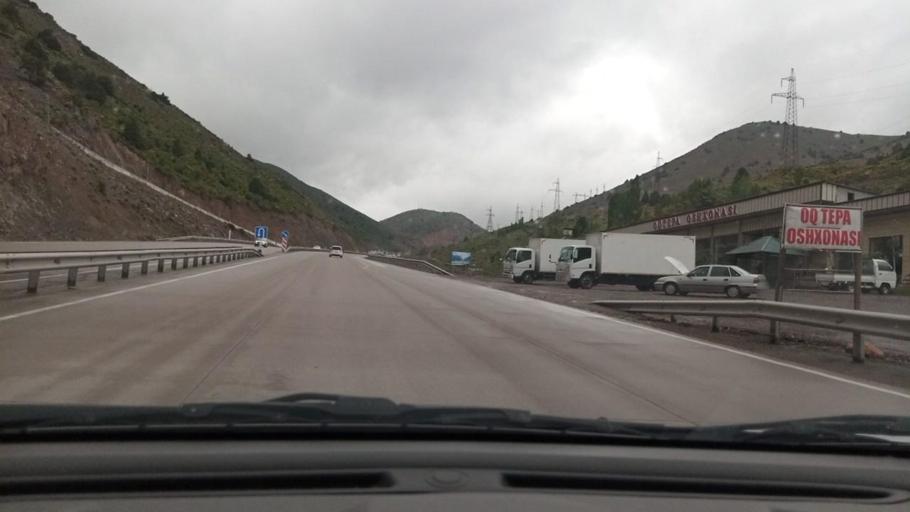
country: UZ
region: Toshkent
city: Angren
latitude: 41.0501
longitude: 70.5689
